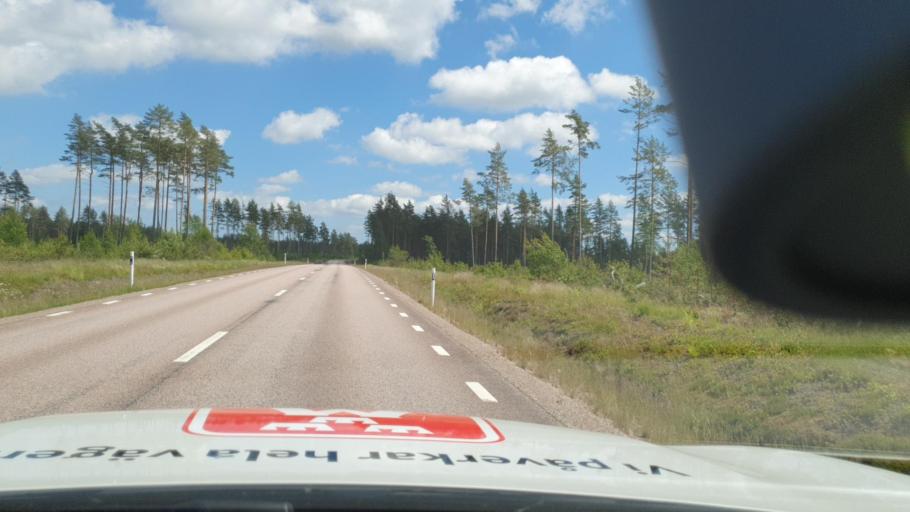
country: SE
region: Vaermland
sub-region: Karlstads Kommun
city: Molkom
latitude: 59.6205
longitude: 13.9099
